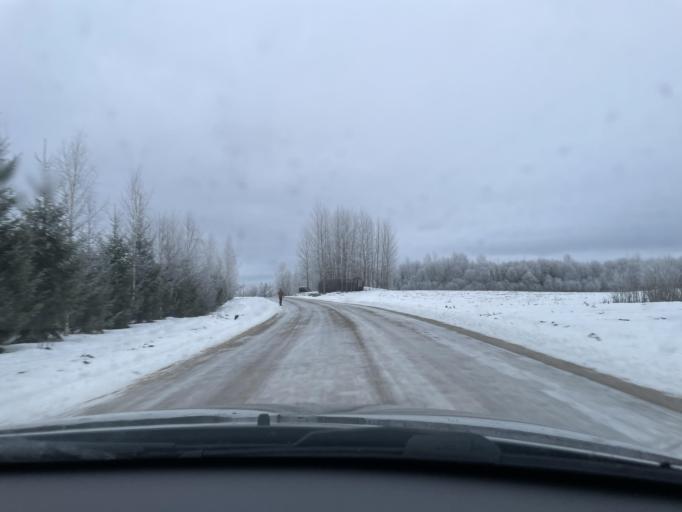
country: LV
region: Ludzas Rajons
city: Ludza
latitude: 56.4588
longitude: 27.5679
